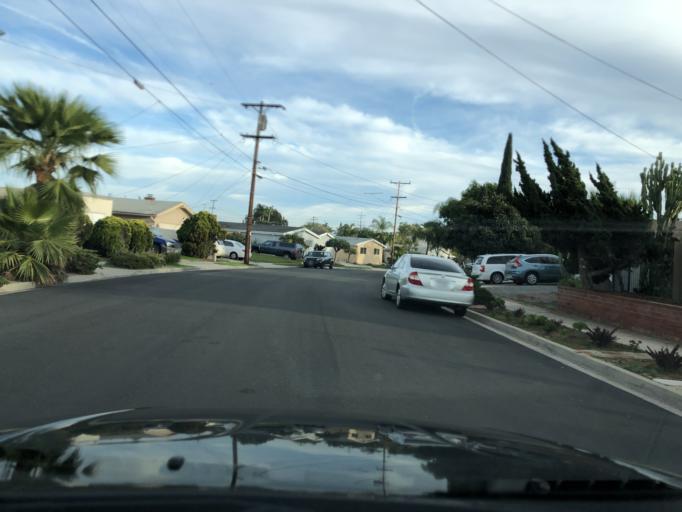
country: US
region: California
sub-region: San Diego County
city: La Jolla
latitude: 32.8271
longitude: -117.1889
